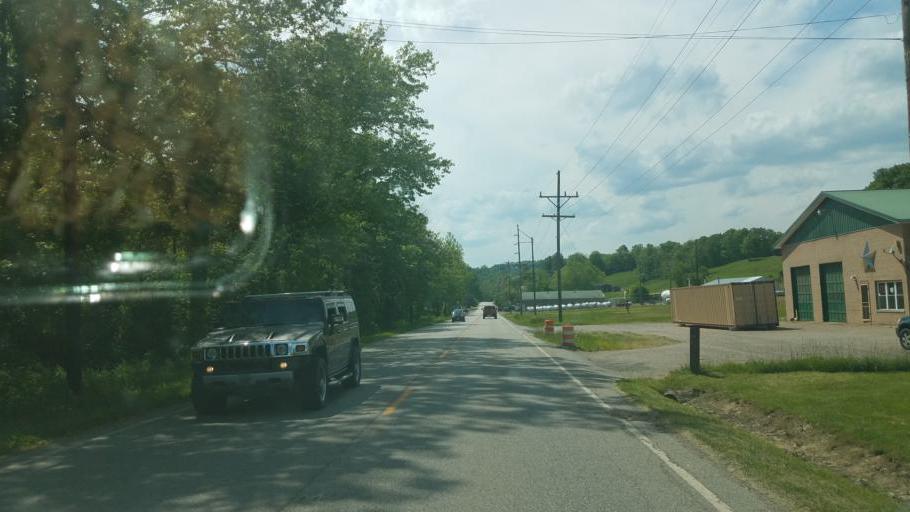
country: US
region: Ohio
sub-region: Meigs County
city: Middleport
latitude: 39.0334
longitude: -82.1192
